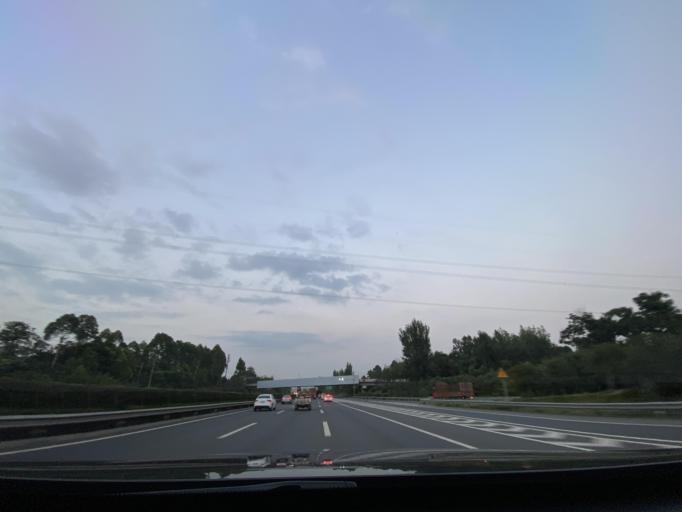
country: CN
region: Sichuan
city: Chengdu
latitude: 30.5703
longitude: 104.1122
